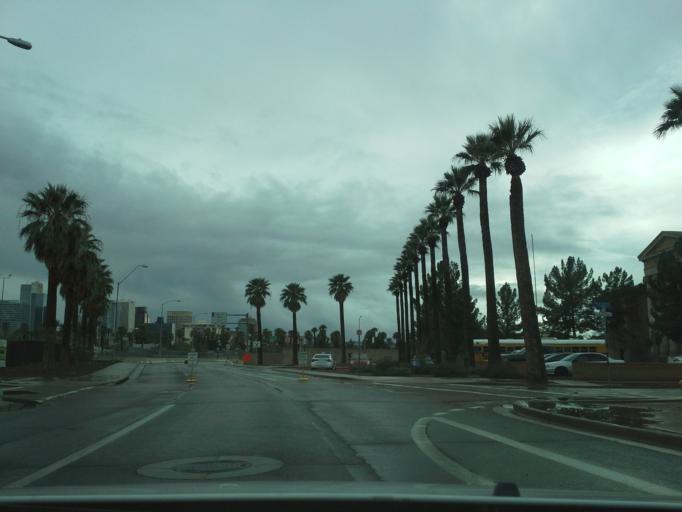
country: US
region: Arizona
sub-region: Maricopa County
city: Phoenix
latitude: 33.4630
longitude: -112.0803
